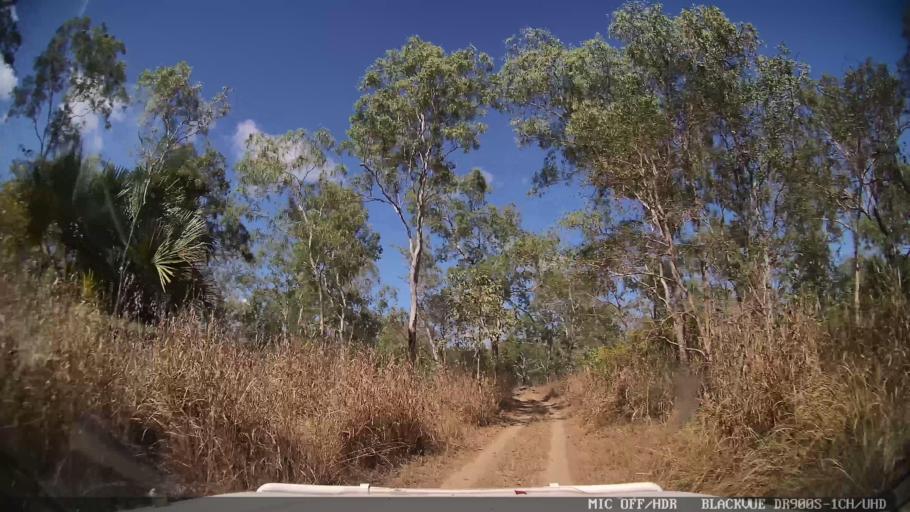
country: AU
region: Queensland
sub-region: Cook
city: Cooktown
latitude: -15.1976
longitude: 144.4289
